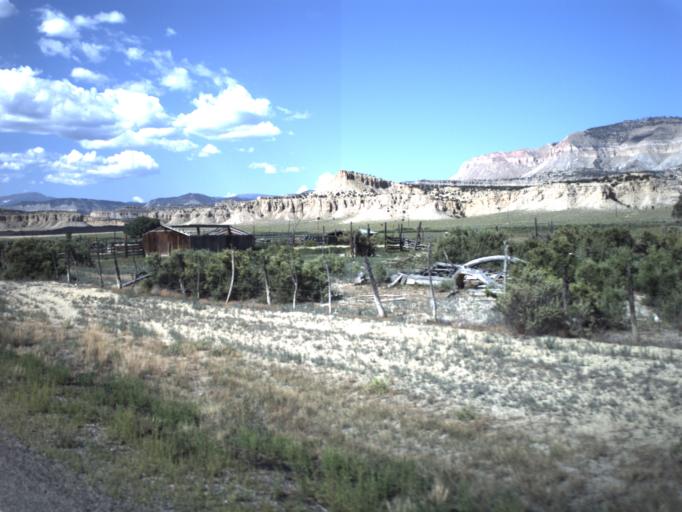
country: US
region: Utah
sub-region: Emery County
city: Ferron
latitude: 38.8710
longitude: -111.2945
